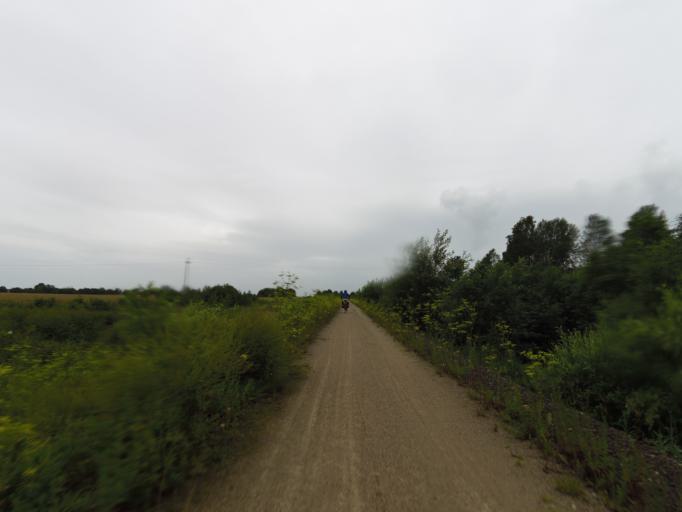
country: EE
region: Laeaene
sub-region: Ridala Parish
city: Uuemoisa
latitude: 58.9542
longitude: 23.8203
